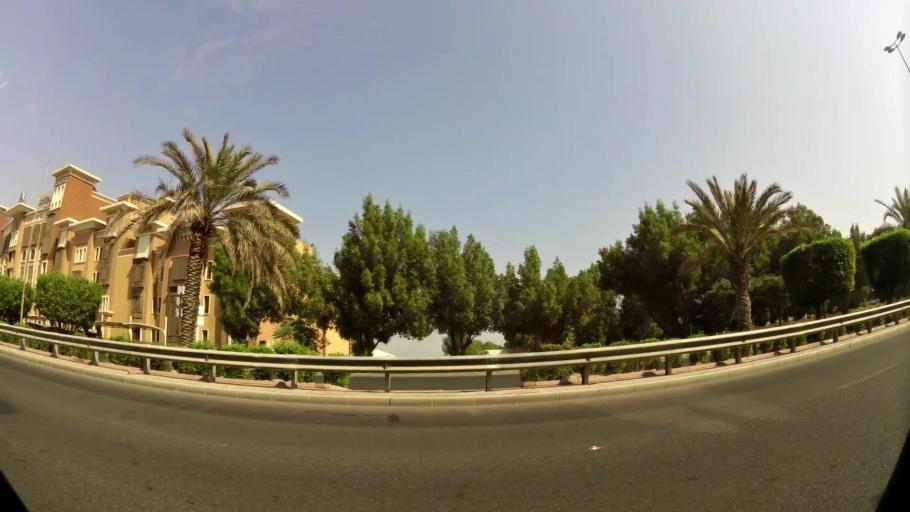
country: KW
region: Al Ahmadi
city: Al Fintas
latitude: 29.1839
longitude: 48.1177
